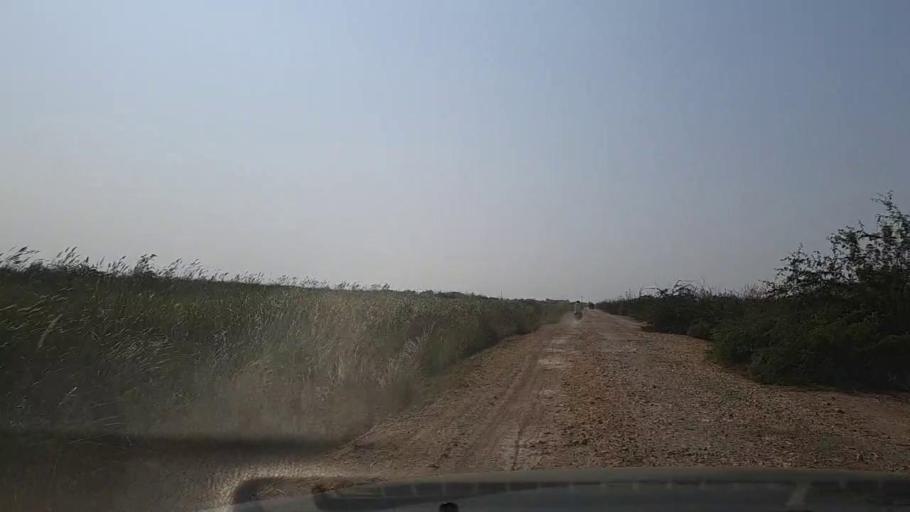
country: PK
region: Sindh
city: Mirpur Sakro
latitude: 24.3704
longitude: 67.6498
